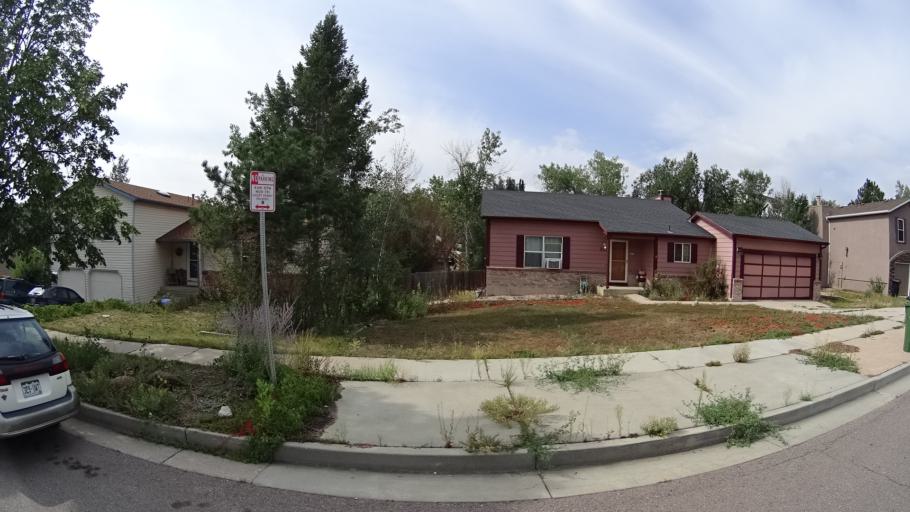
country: US
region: Colorado
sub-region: El Paso County
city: Colorado Springs
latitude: 38.8911
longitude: -104.7900
